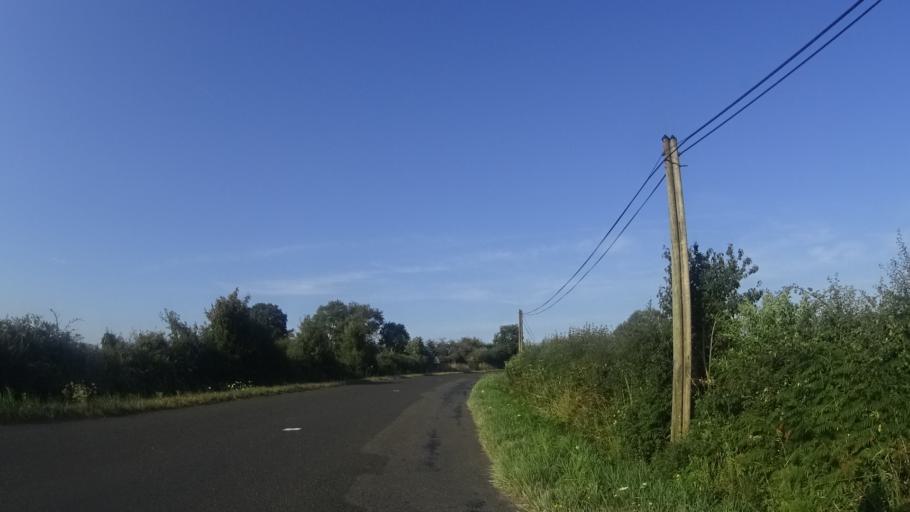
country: FR
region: Pays de la Loire
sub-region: Departement de la Loire-Atlantique
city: Riaille
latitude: 47.4995
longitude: -1.3096
